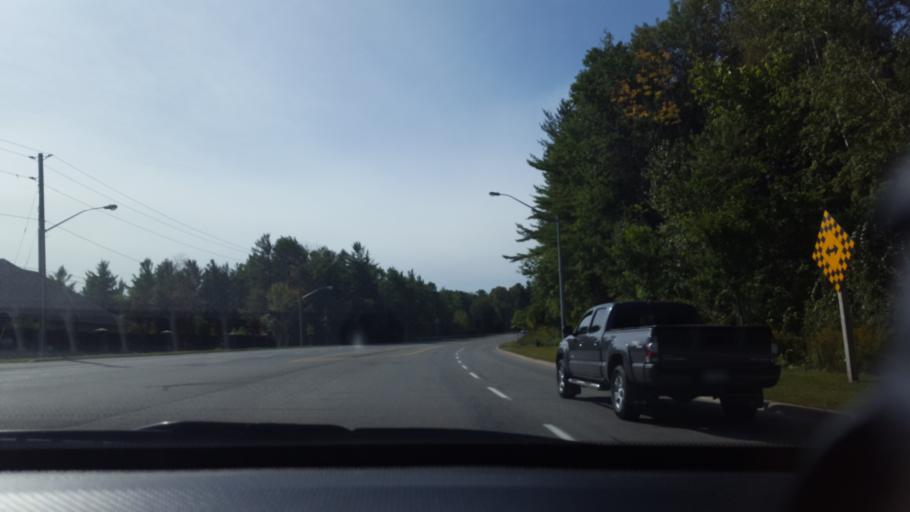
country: CA
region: Ontario
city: Newmarket
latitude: 44.0279
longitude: -79.4957
